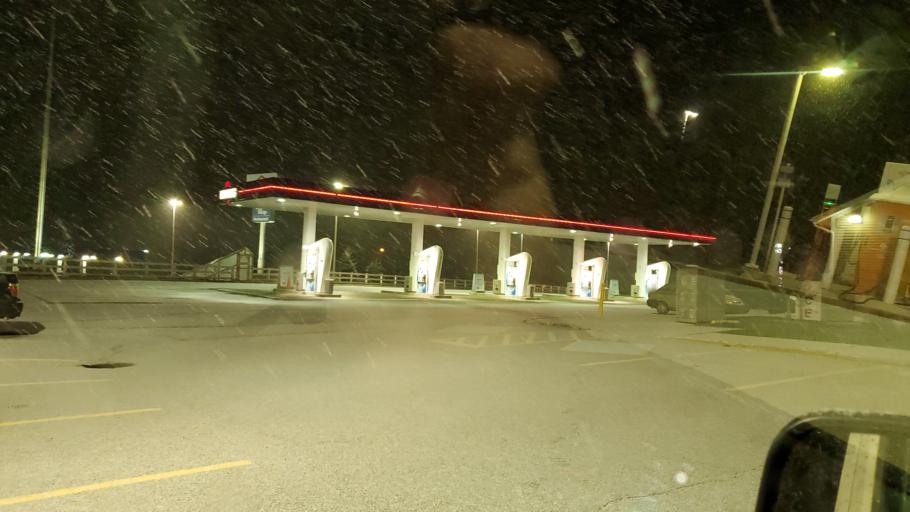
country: US
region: Maine
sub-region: Aroostook County
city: Limestone
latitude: 47.0768
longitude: -67.7672
